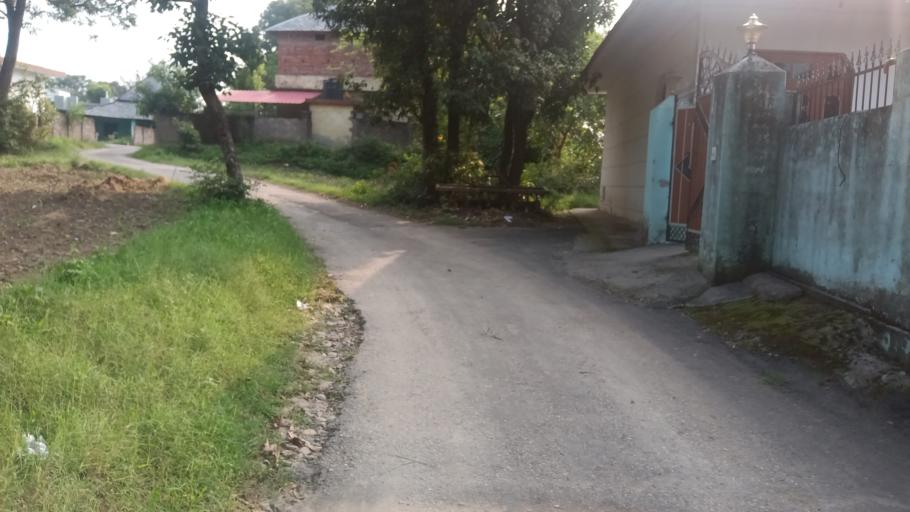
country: IN
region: Himachal Pradesh
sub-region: Hamirpur
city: Nadaun
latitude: 31.6915
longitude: 76.3557
